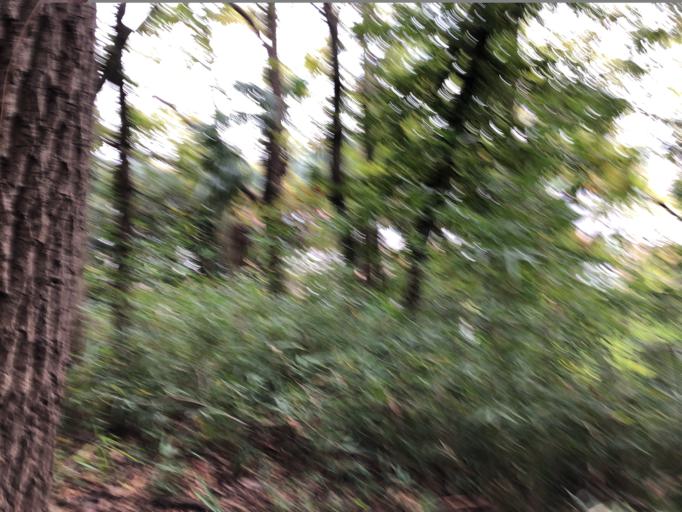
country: JP
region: Tokyo
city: Hino
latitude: 35.6205
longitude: 139.3867
